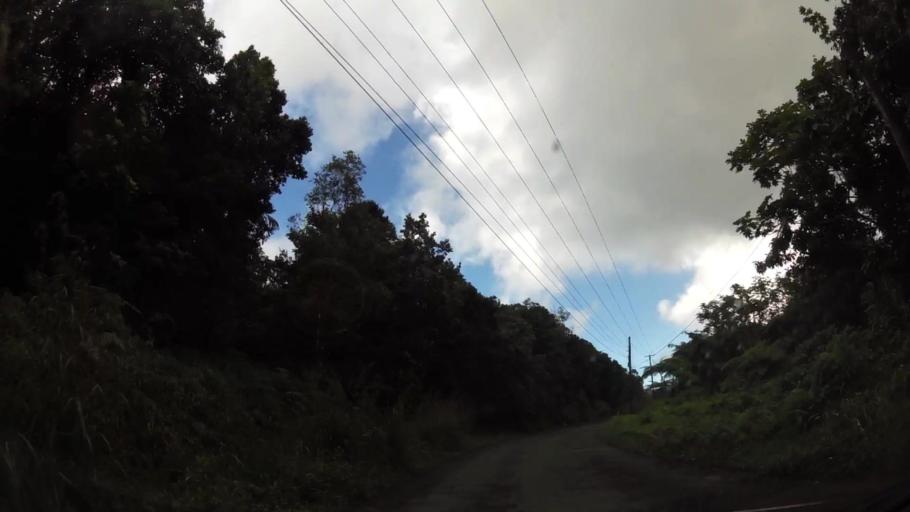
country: DM
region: Saint Paul
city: Pont Casse
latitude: 15.3905
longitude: -61.3143
